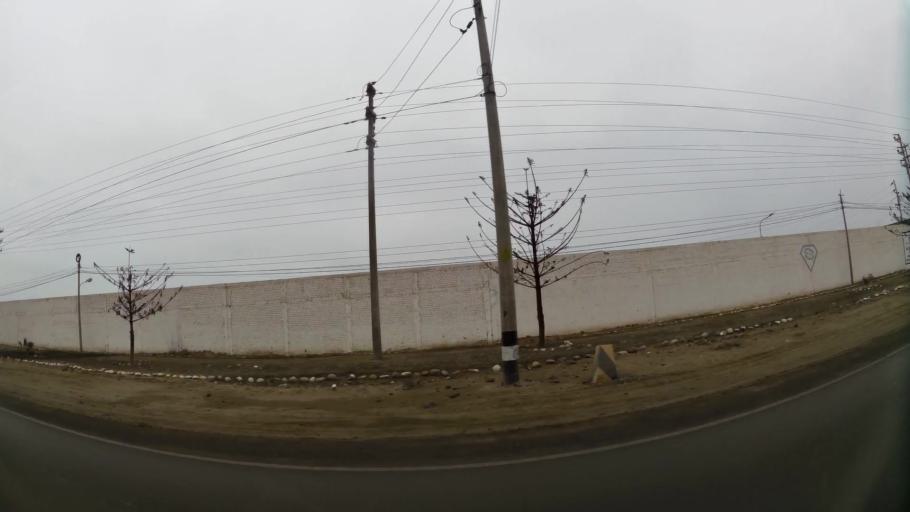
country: PE
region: Ica
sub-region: Provincia de Pisco
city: Paracas
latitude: -13.7919
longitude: -76.2396
